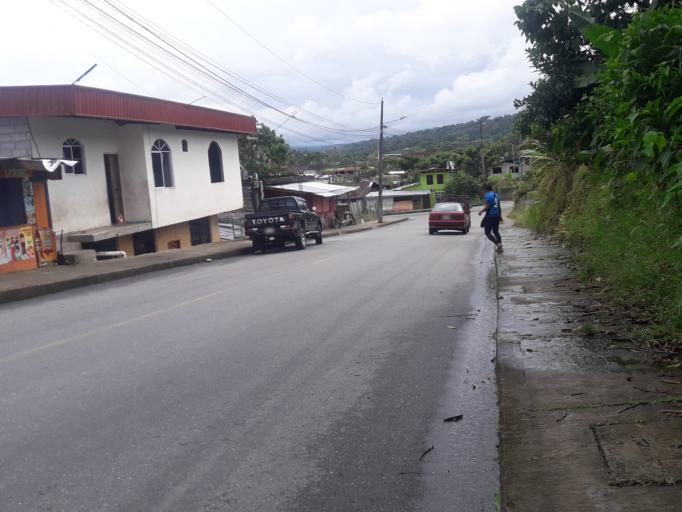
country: EC
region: Napo
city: Tena
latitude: -0.9954
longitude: -77.8088
